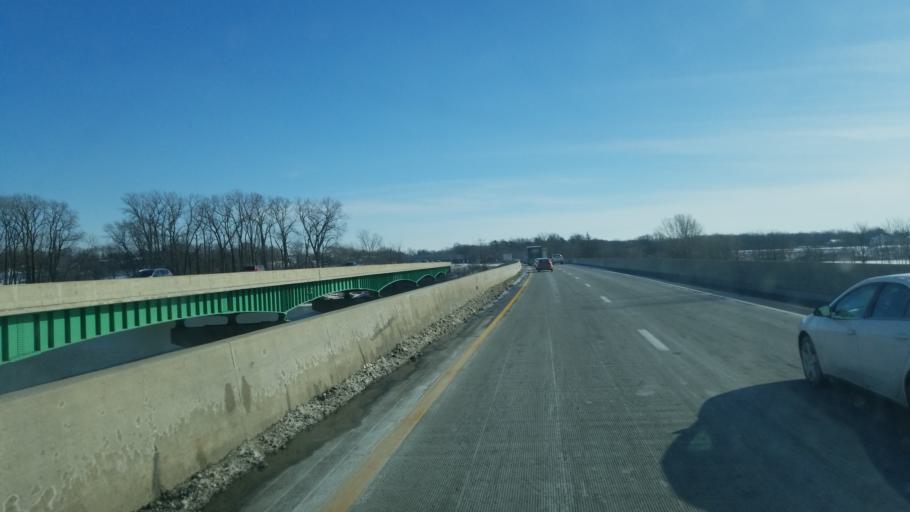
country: US
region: Ohio
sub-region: Lucas County
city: Maumee
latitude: 41.5467
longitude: -83.6836
